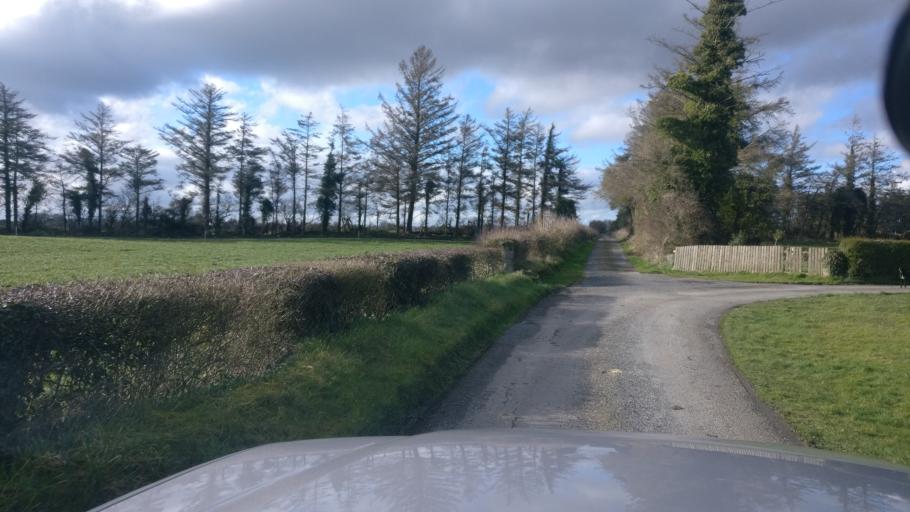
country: IE
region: Connaught
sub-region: County Galway
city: Loughrea
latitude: 53.2077
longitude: -8.4218
